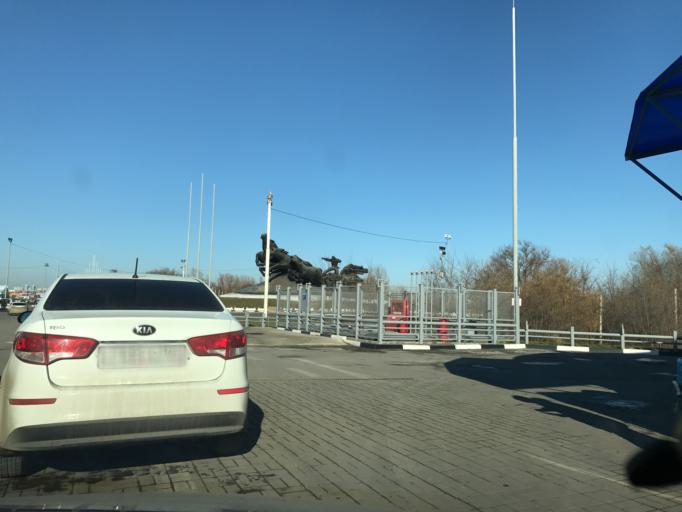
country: RU
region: Rostov
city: Bataysk
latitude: 47.1831
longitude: 39.7388
